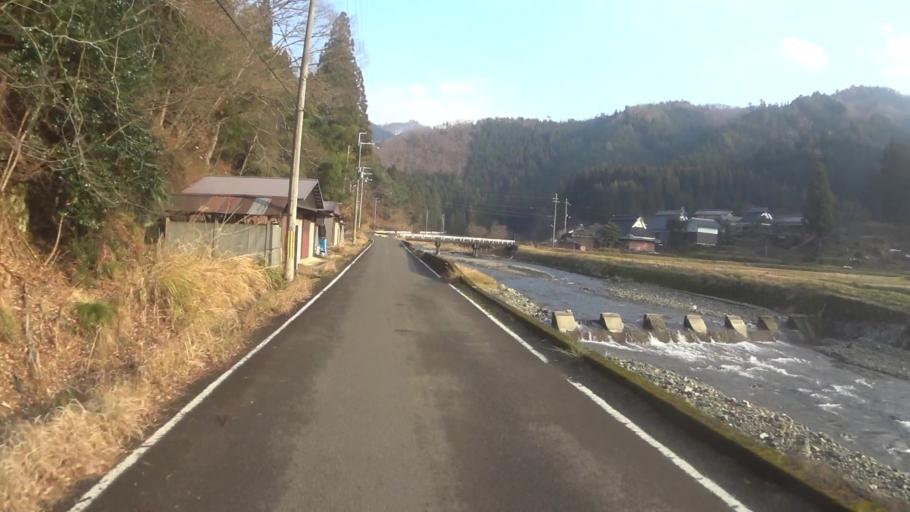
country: JP
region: Kyoto
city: Maizuru
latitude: 35.3680
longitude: 135.4554
